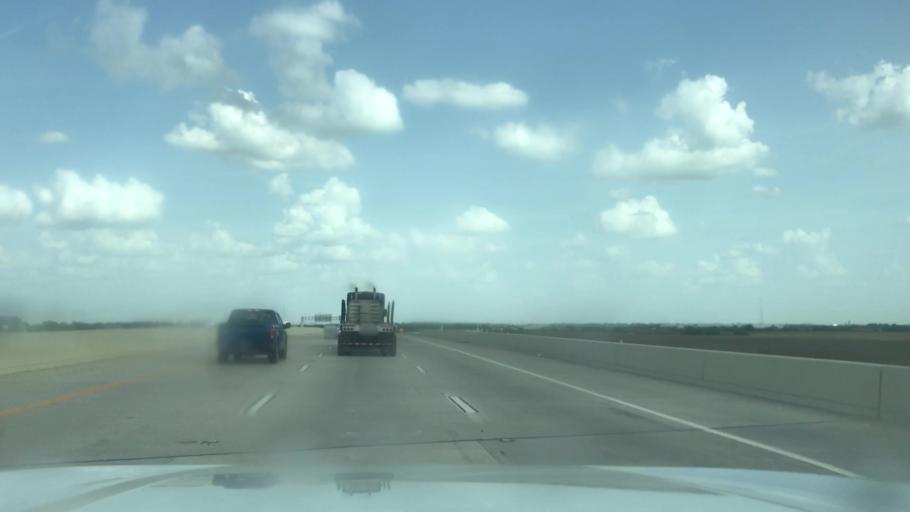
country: US
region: Texas
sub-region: Waller County
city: Waller
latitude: 30.0576
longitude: -95.8918
